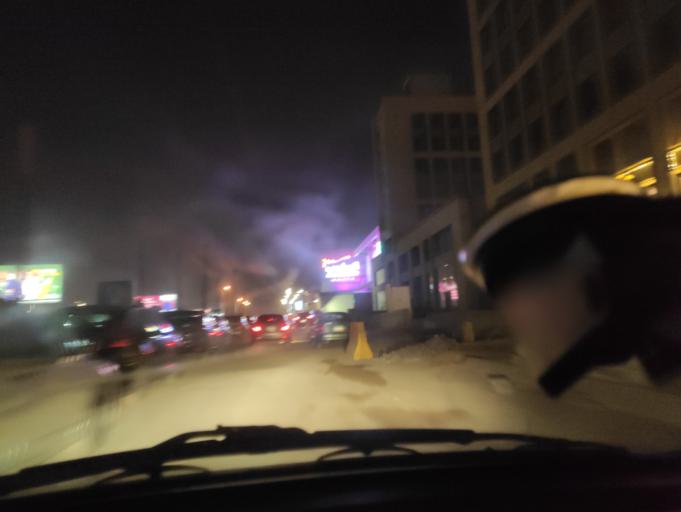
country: EG
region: Al Jizah
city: Awsim
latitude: 30.0189
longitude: 31.0056
